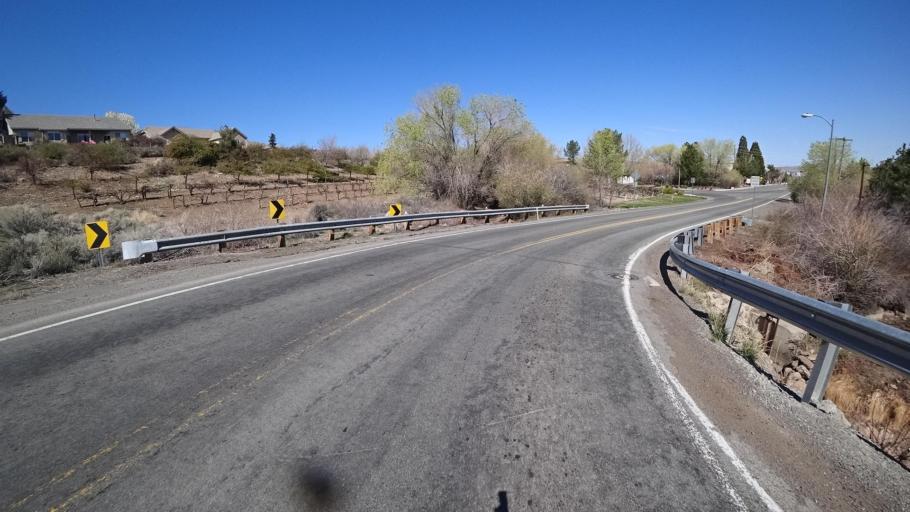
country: US
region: Nevada
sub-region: Washoe County
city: Reno
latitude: 39.4685
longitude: -119.8078
